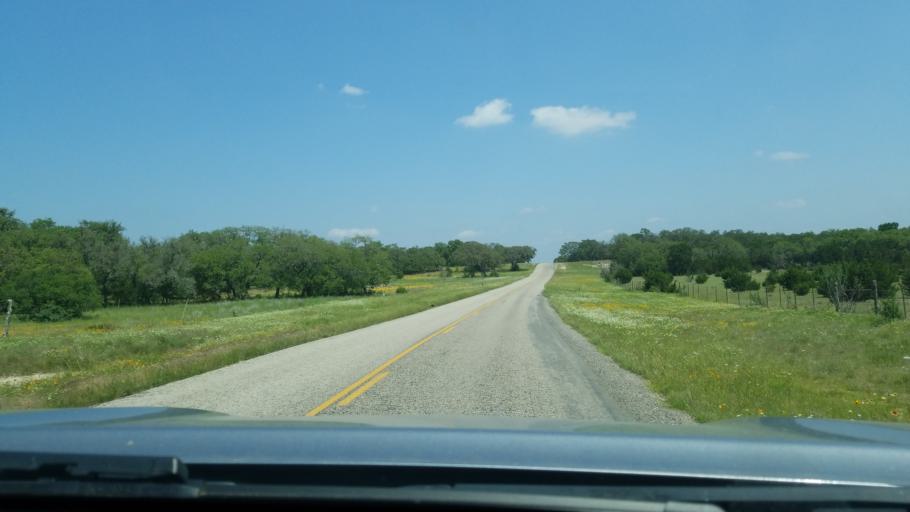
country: US
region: Texas
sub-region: Blanco County
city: Blanco
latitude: 29.9750
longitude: -98.5376
